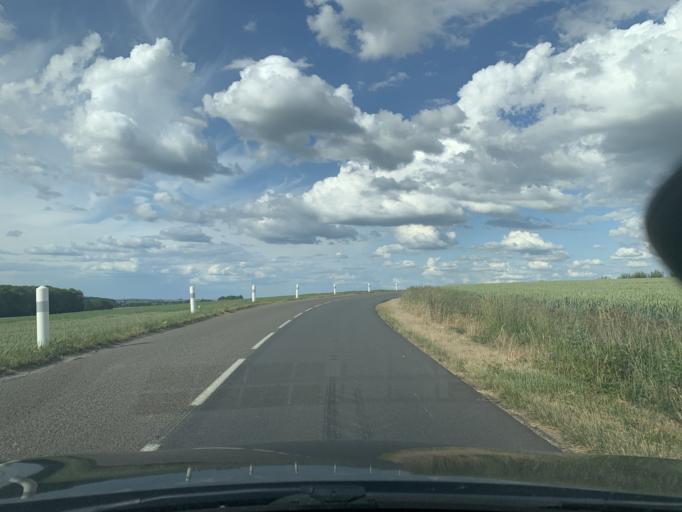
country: FR
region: Nord-Pas-de-Calais
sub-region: Departement du Nord
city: Marcoing
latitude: 50.0973
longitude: 3.1552
